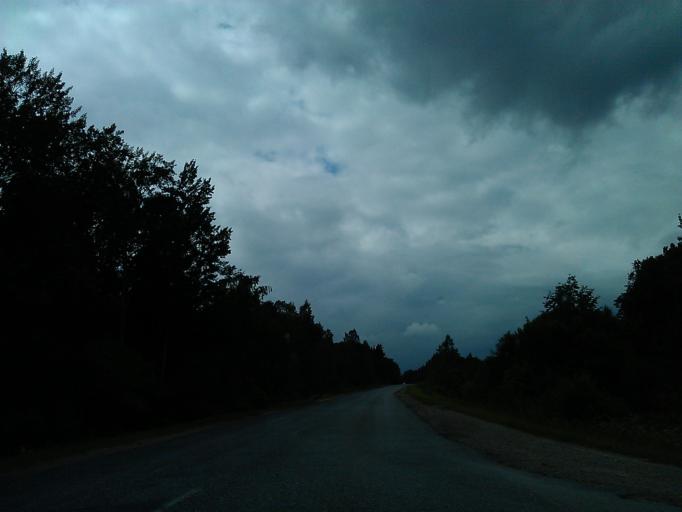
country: LV
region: Kuldigas Rajons
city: Kuldiga
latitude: 56.9826
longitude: 22.0478
